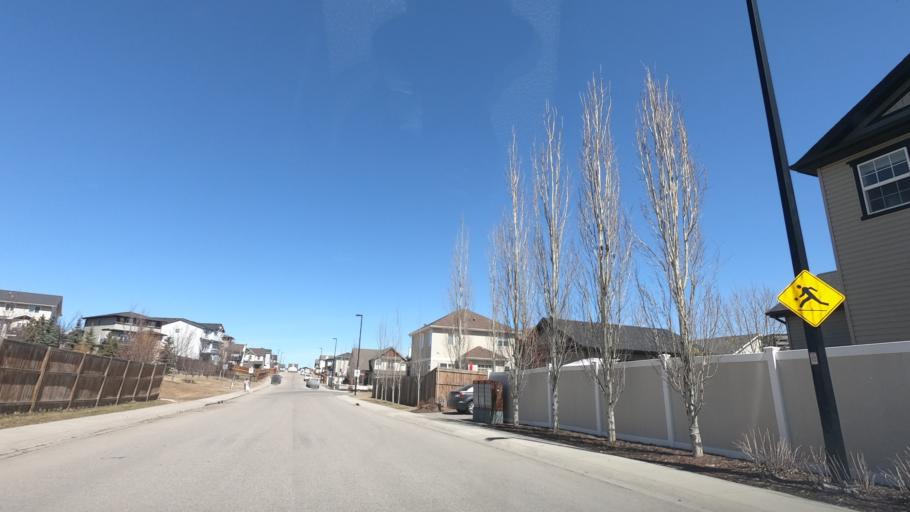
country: CA
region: Alberta
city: Airdrie
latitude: 51.3024
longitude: -114.0469
